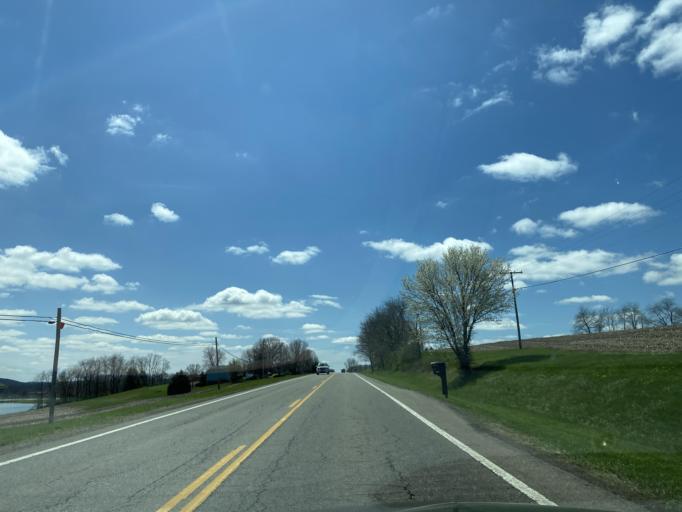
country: US
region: Ohio
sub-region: Wayne County
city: Wooster
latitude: 40.7498
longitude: -81.9819
